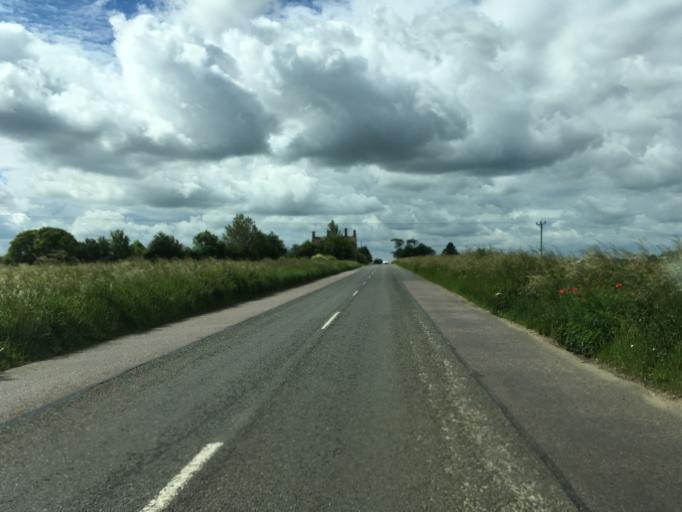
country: GB
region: England
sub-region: Oxfordshire
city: Shipton under Wychwood
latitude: 51.8307
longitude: -1.6095
